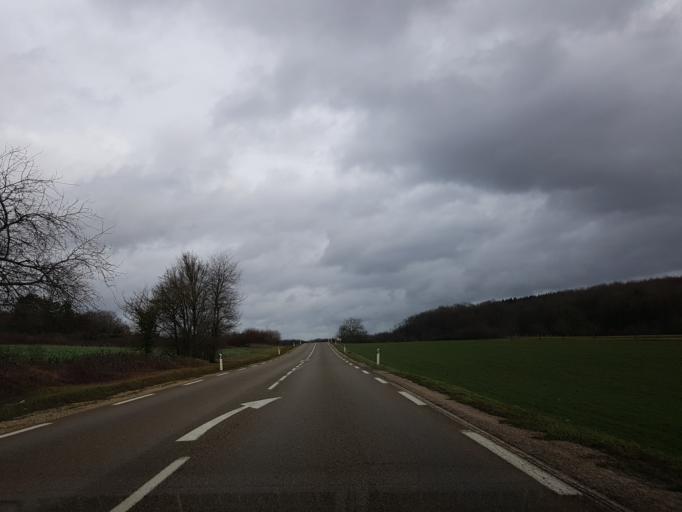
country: FR
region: Franche-Comte
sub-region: Departement de la Haute-Saone
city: Jussey
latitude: 47.7210
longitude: 5.8522
